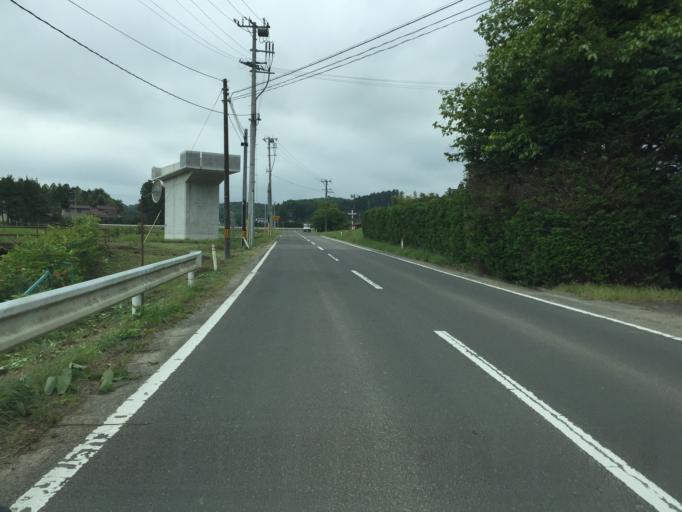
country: JP
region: Miyagi
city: Marumori
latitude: 37.7748
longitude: 140.8956
